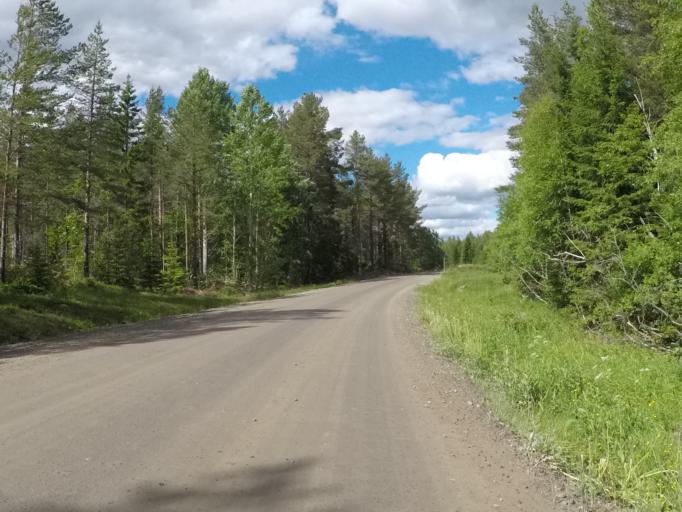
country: SE
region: Vaesterbotten
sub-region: Robertsfors Kommun
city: Robertsfors
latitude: 64.1332
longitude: 20.9046
